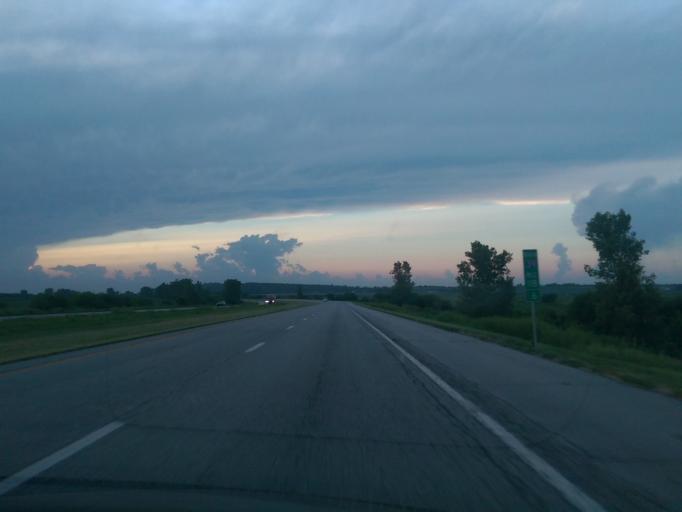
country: US
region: Iowa
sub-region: Fremont County
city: Hamburg
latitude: 40.5138
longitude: -95.6023
